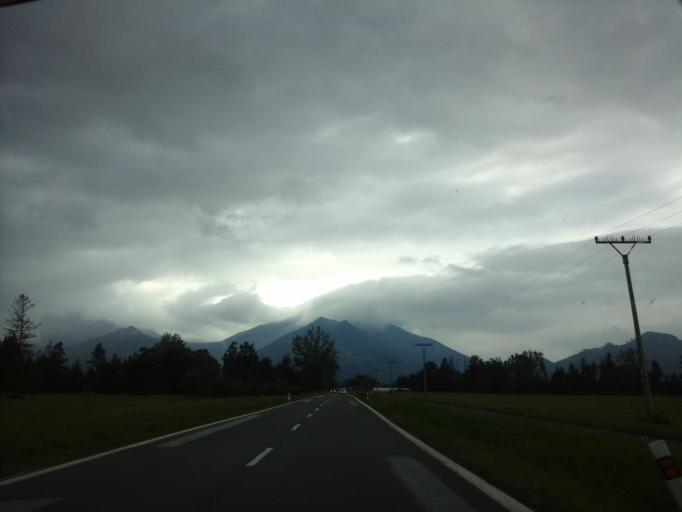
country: SK
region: Presovsky
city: Spisska Bela
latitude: 49.2087
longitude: 20.3804
